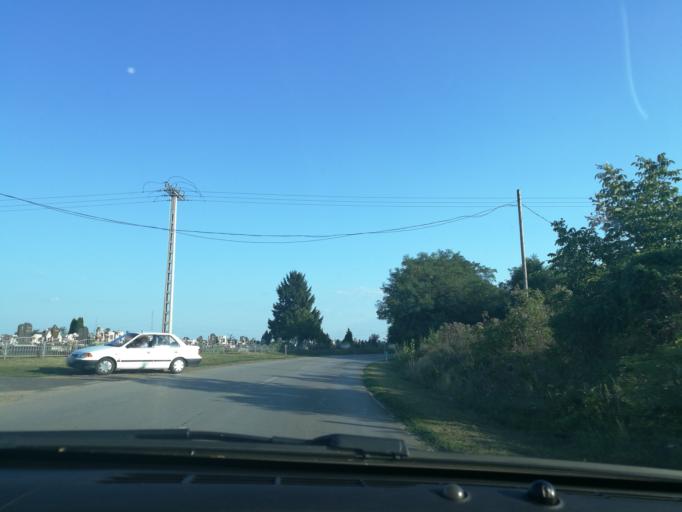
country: HU
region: Szabolcs-Szatmar-Bereg
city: Buj
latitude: 48.0902
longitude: 21.6412
